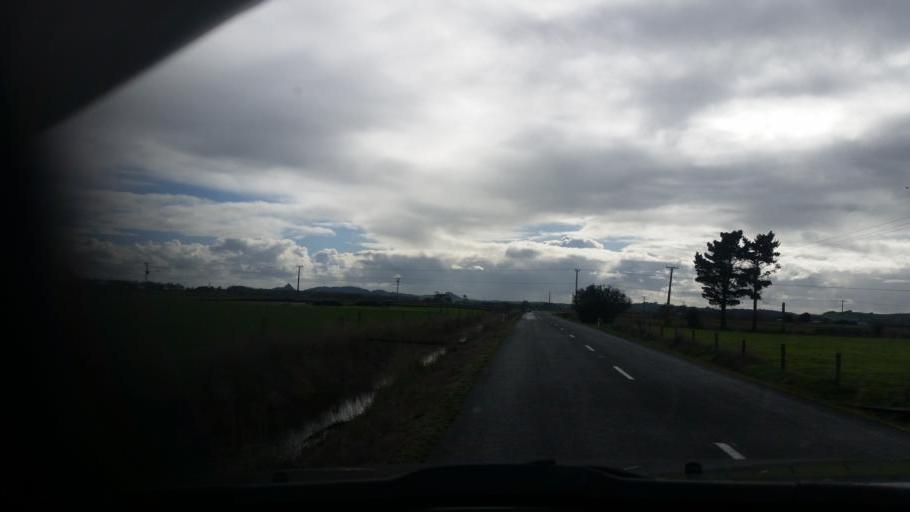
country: NZ
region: Northland
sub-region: Kaipara District
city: Dargaville
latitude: -36.1252
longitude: 174.0515
